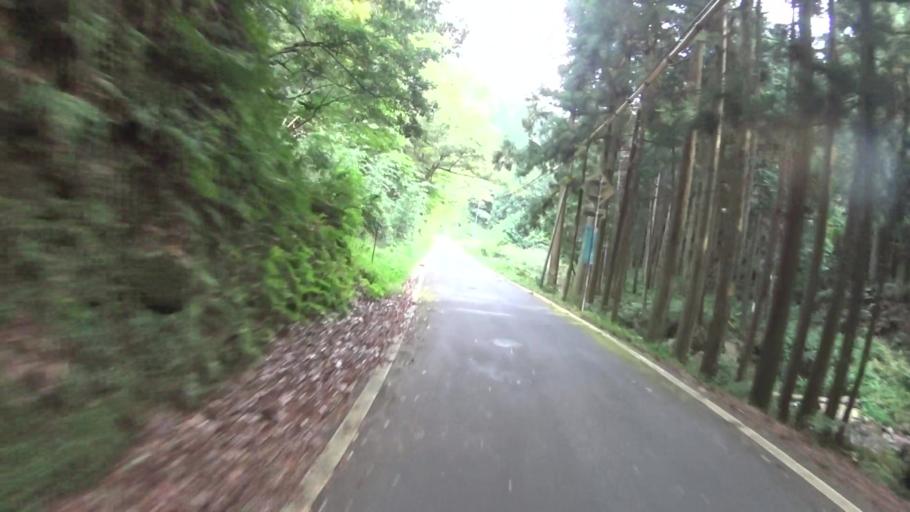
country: JP
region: Kyoto
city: Miyazu
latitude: 35.6102
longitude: 135.2070
